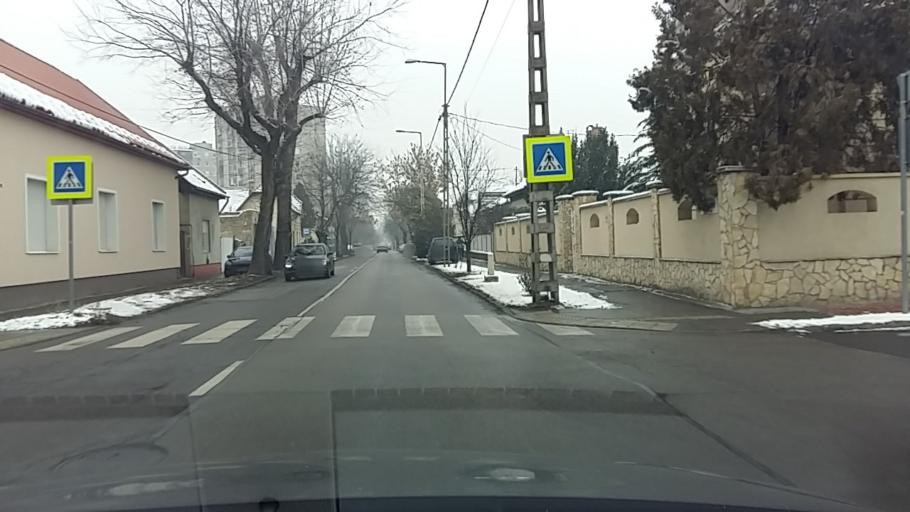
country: HU
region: Budapest
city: Budapest XV. keruelet
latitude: 47.5575
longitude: 19.1057
